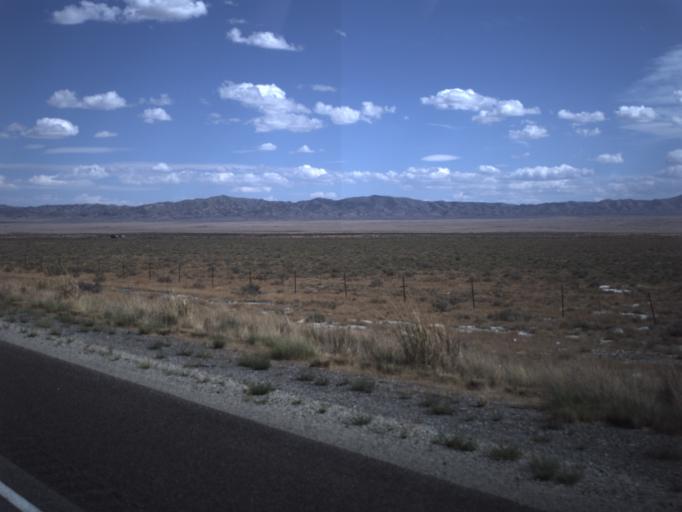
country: US
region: Utah
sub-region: Tooele County
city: Grantsville
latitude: 40.7279
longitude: -113.1268
